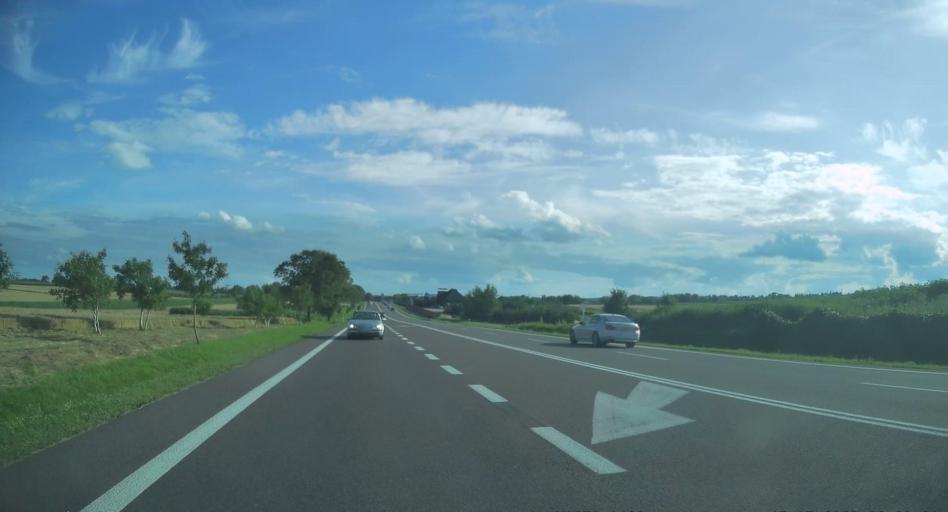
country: PL
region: Subcarpathian Voivodeship
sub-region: Powiat przemyski
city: Orly
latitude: 49.8505
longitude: 22.8043
